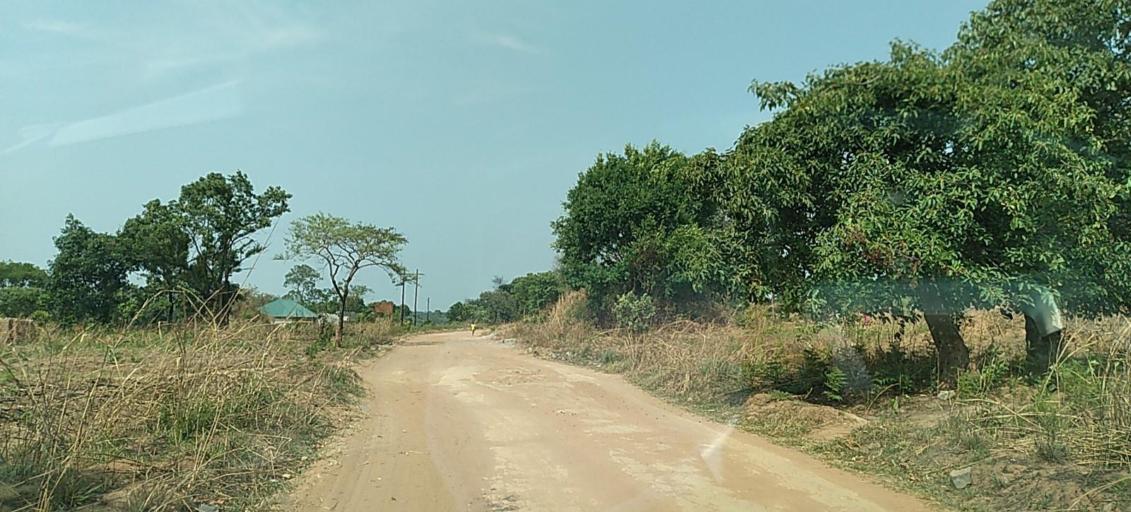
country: ZM
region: Copperbelt
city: Chililabombwe
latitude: -12.3353
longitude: 27.7277
